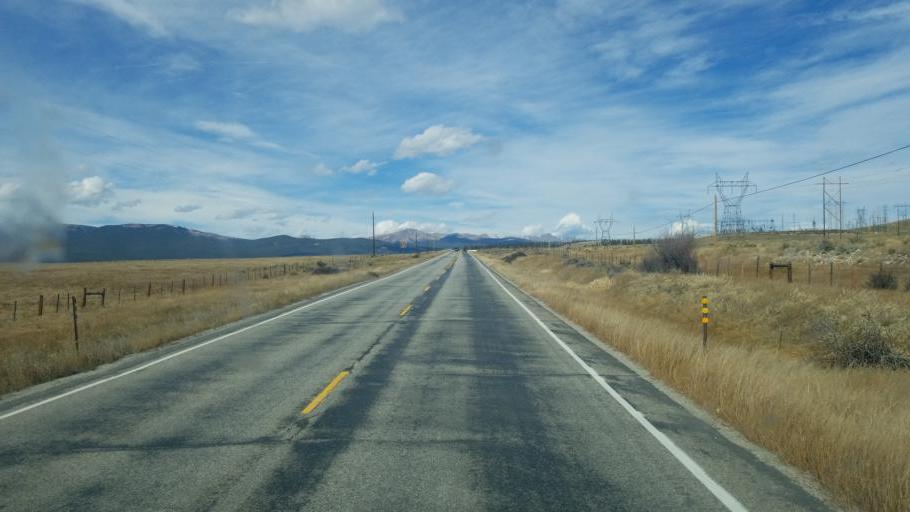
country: US
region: Colorado
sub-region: Lake County
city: Leadville
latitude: 39.1801
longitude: -106.3257
